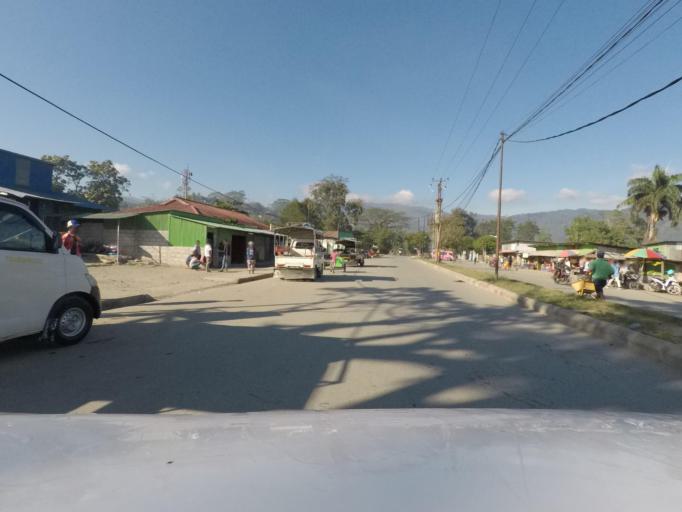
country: TL
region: Ermera
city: Gleno
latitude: -8.7233
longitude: 125.4361
